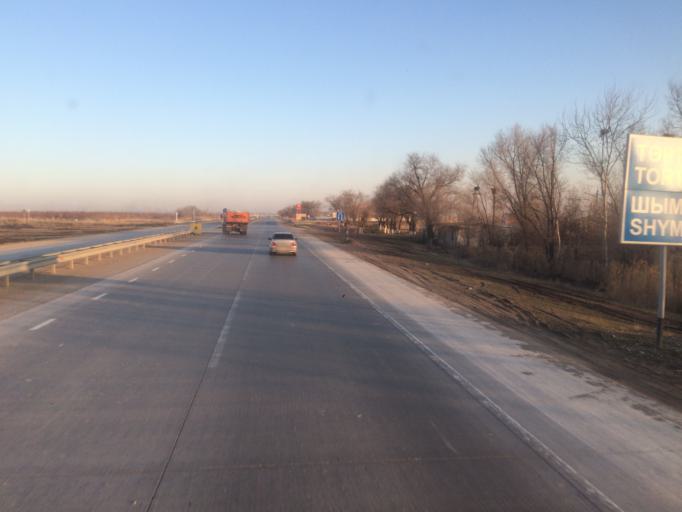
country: KZ
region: Ongtustik Qazaqstan
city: Turkestan
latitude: 43.2710
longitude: 68.3475
